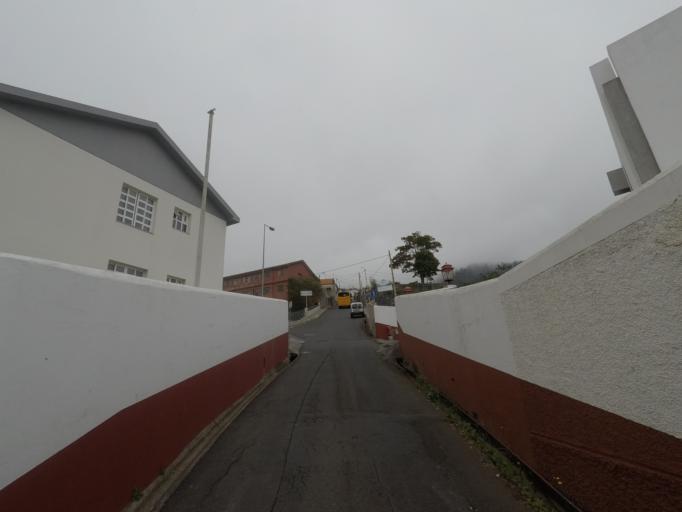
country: PT
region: Madeira
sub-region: Funchal
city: Nossa Senhora do Monte
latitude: 32.6777
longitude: -16.9464
